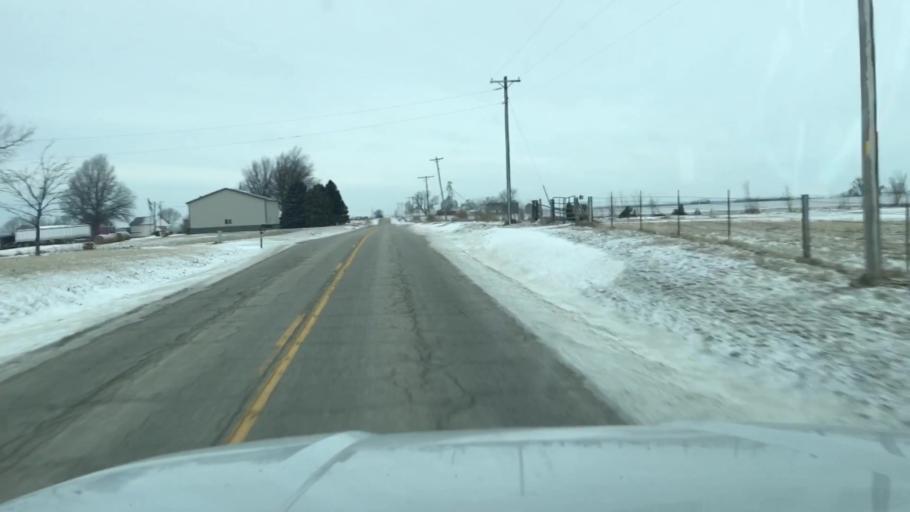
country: US
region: Missouri
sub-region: Andrew County
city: Savannah
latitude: 40.0248
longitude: -94.9308
